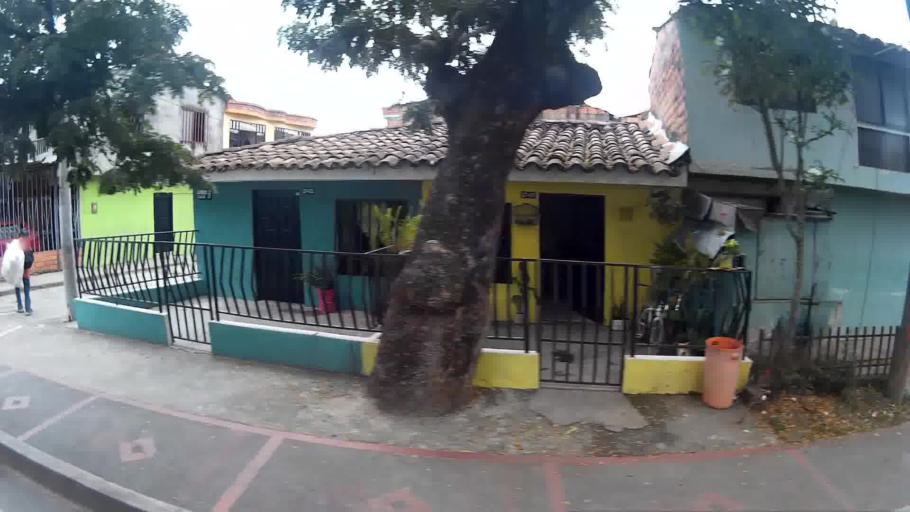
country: CO
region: Risaralda
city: La Virginia
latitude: 4.9032
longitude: -75.8781
